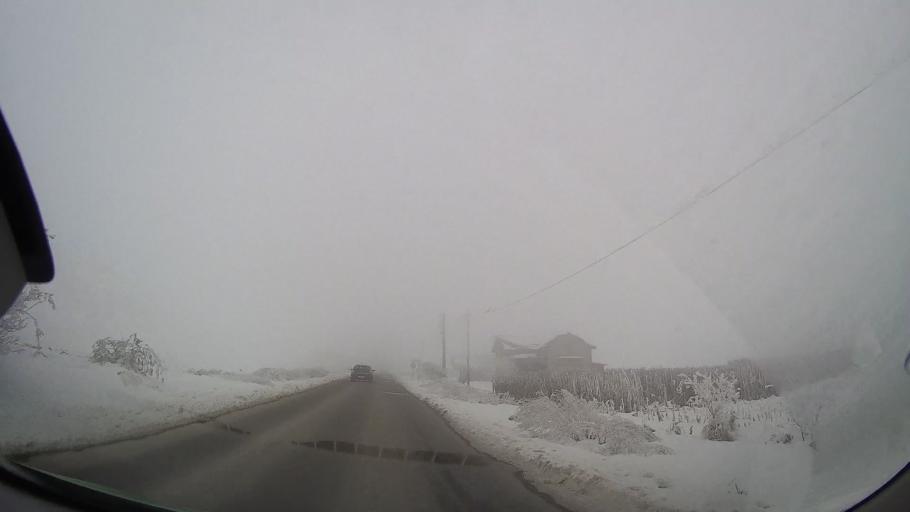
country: RO
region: Neamt
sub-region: Comuna Sabaoani
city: Sabaoani
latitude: 46.9958
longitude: 26.8631
